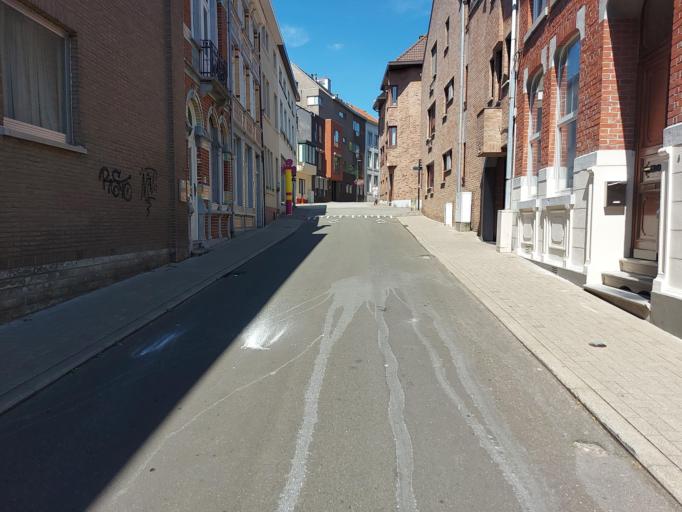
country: BE
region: Flanders
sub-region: Provincie Limburg
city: Tongeren
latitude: 50.7786
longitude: 5.4638
